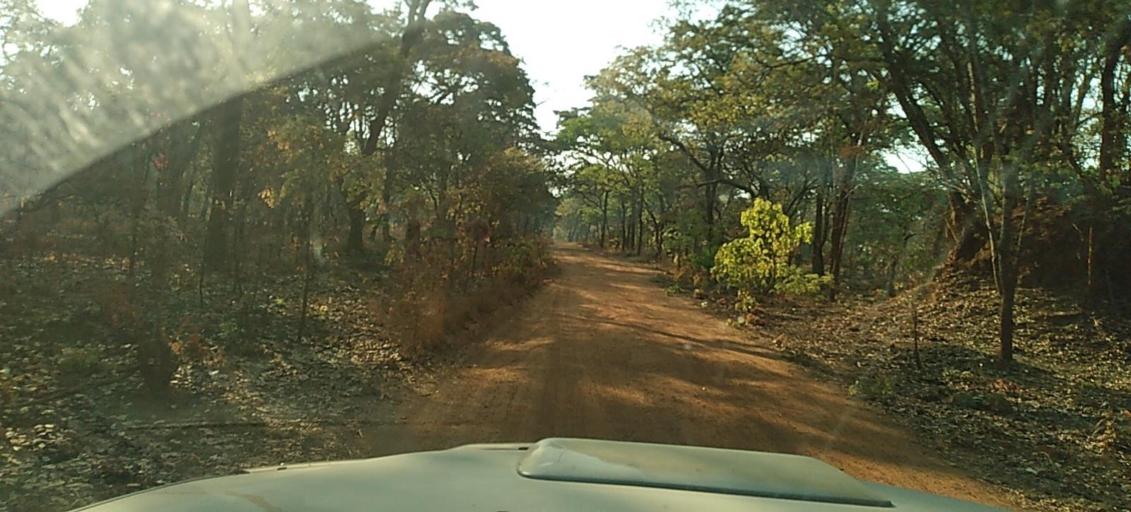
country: ZM
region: North-Western
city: Kasempa
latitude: -13.1683
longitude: 25.8940
